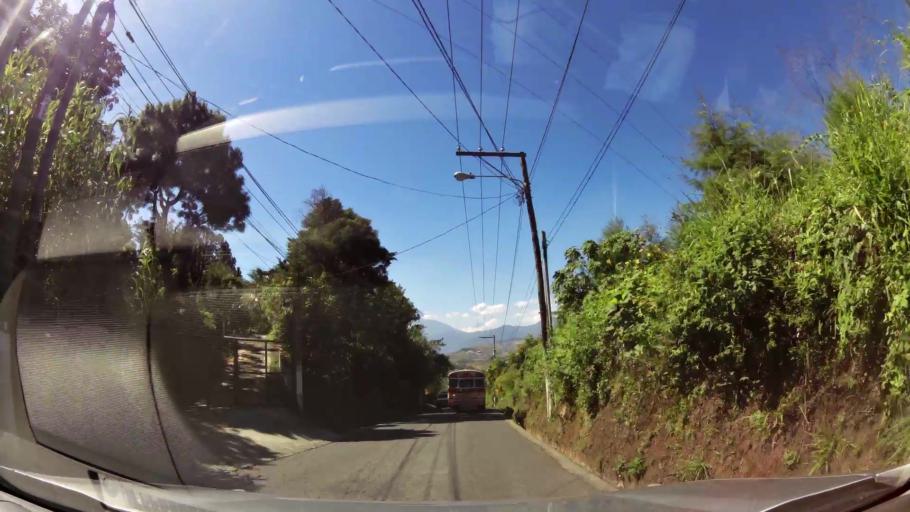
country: GT
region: Guatemala
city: Villa Canales
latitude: 14.4871
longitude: -90.5275
